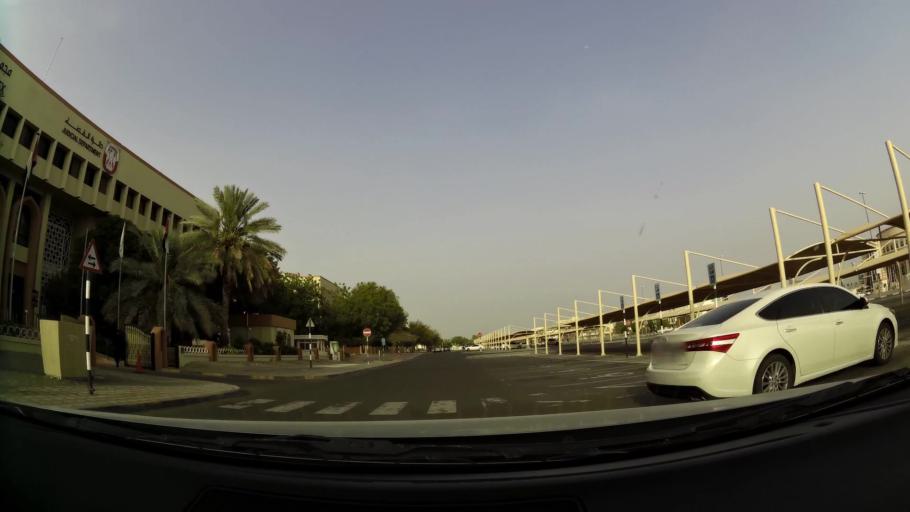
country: AE
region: Abu Dhabi
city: Al Ain
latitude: 24.2374
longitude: 55.7321
